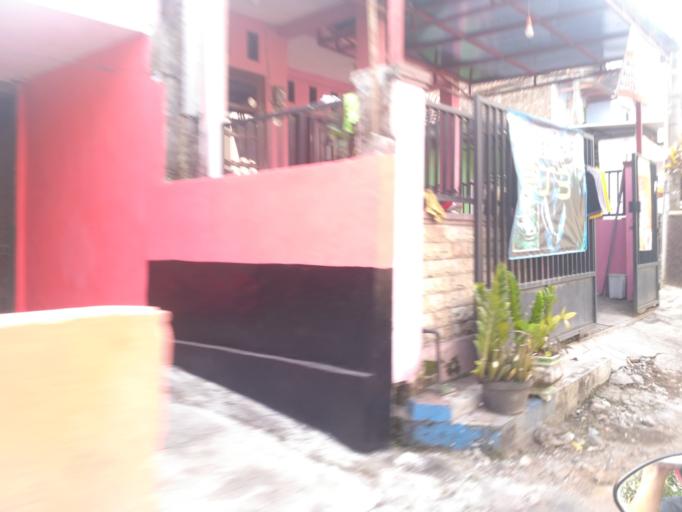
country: ID
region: East Java
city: Malang
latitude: -7.9593
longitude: 112.6276
